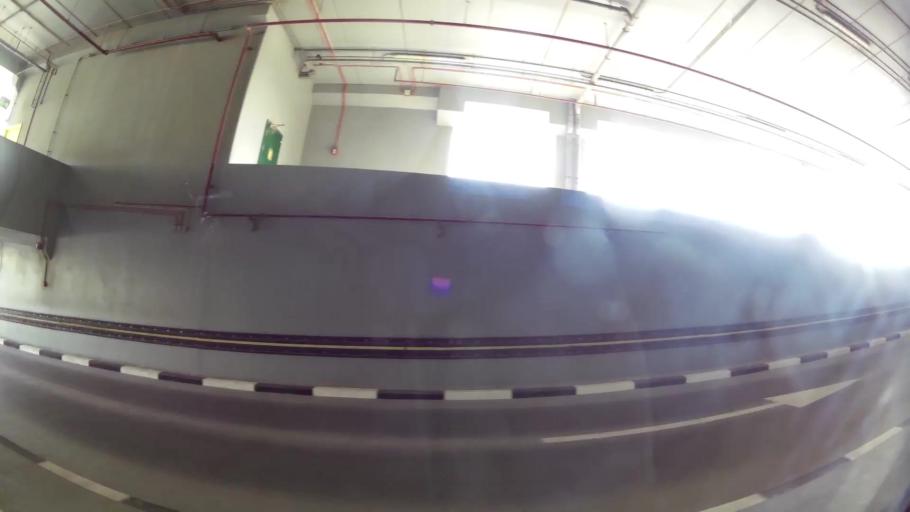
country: AE
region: Ash Shariqah
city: Sharjah
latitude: 25.2559
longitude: 55.4014
